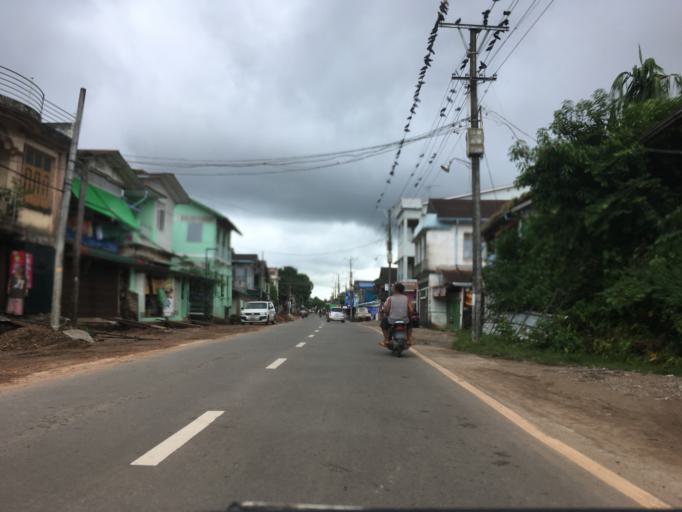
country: MM
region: Mon
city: Mawlamyine
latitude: 16.4616
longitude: 97.6247
